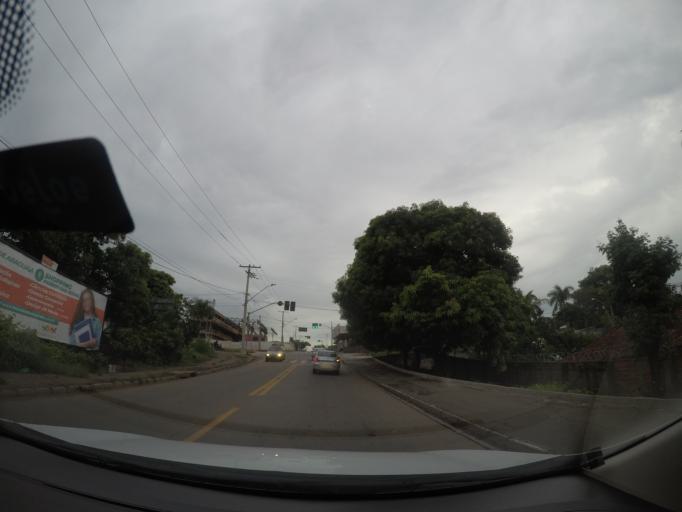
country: BR
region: Goias
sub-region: Goiania
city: Goiania
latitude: -16.6553
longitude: -49.2996
